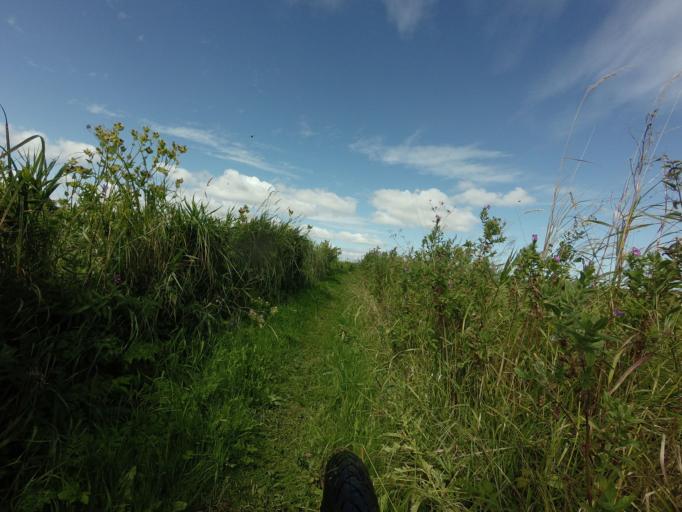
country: DK
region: Central Jutland
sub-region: Norddjurs Kommune
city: Allingabro
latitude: 56.4480
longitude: 10.3550
